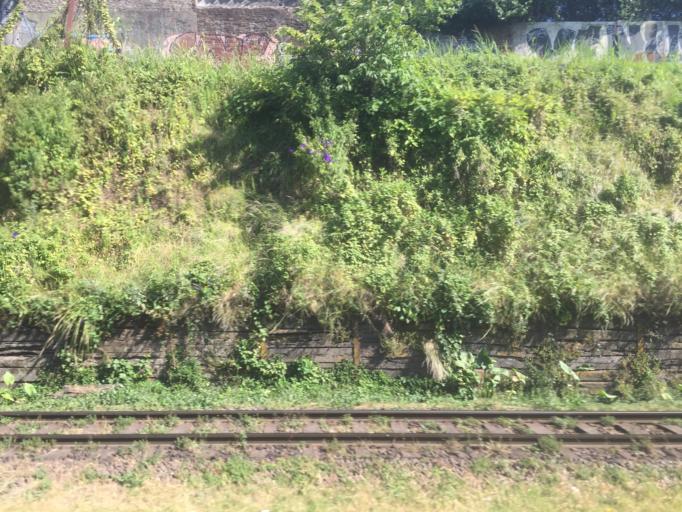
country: AR
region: Buenos Aires
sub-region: Partido de Vicente Lopez
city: Olivos
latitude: -34.5360
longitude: -58.4742
